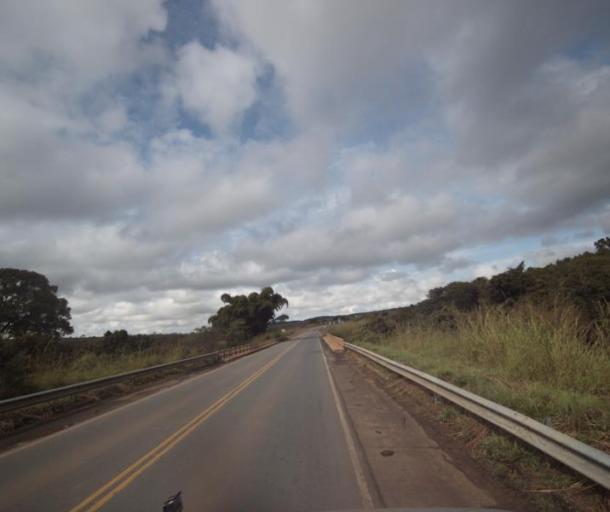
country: BR
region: Goias
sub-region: Pirenopolis
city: Pirenopolis
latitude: -15.8231
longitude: -48.7784
